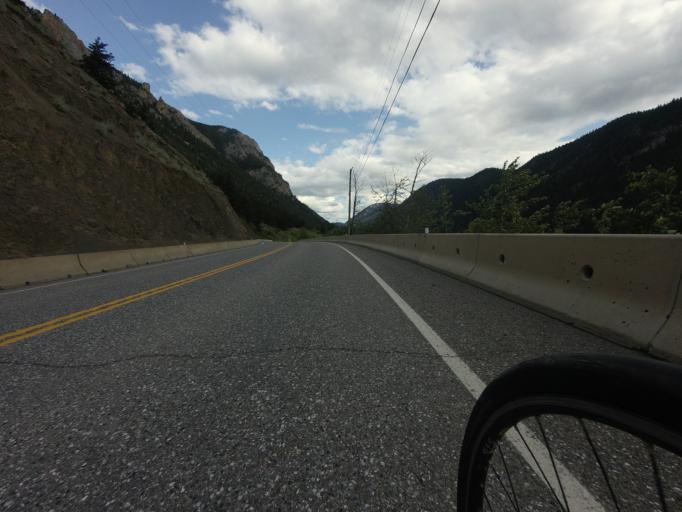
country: CA
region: British Columbia
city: Lillooet
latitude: 50.8669
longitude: -121.7354
